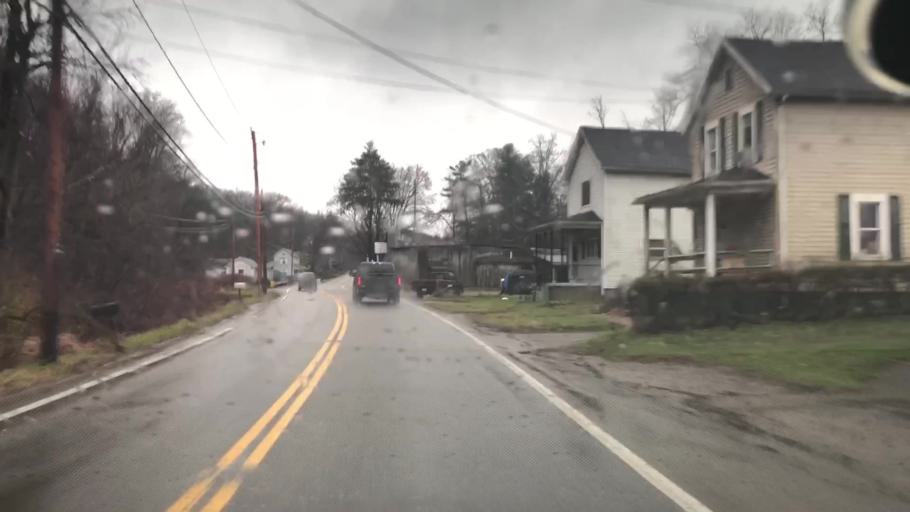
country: US
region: Ohio
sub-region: Belmont County
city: Saint Clairsville
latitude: 40.0946
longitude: -80.9099
